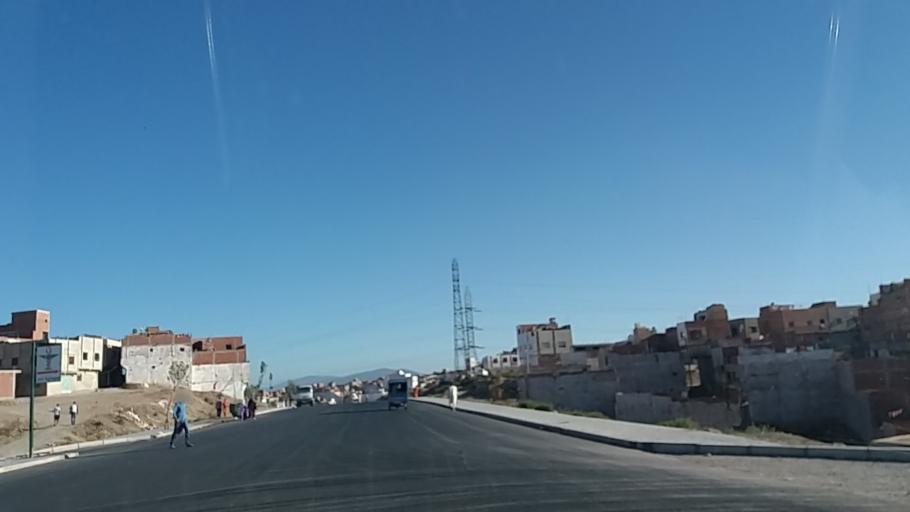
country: MA
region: Tanger-Tetouan
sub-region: Tanger-Assilah
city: Tangier
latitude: 35.7321
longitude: -5.7880
